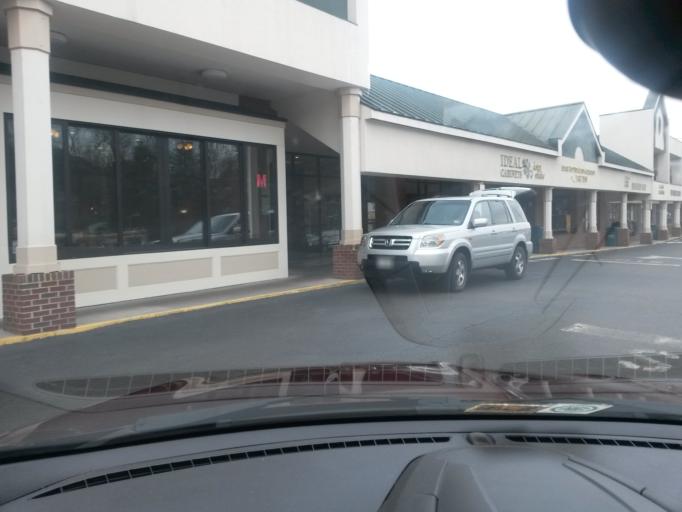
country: US
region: Virginia
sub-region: Roanoke County
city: Narrows
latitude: 37.2346
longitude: -79.9714
